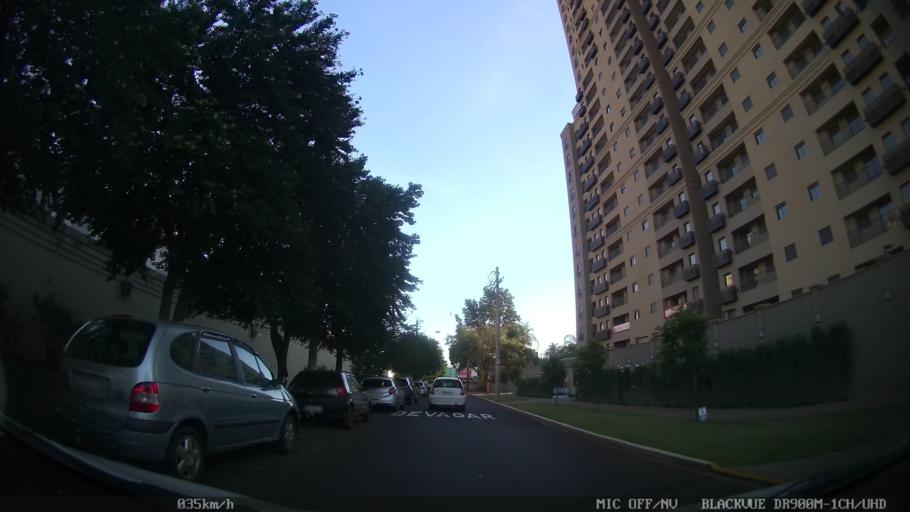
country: BR
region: Sao Paulo
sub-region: Ribeirao Preto
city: Ribeirao Preto
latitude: -21.2067
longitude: -47.7931
